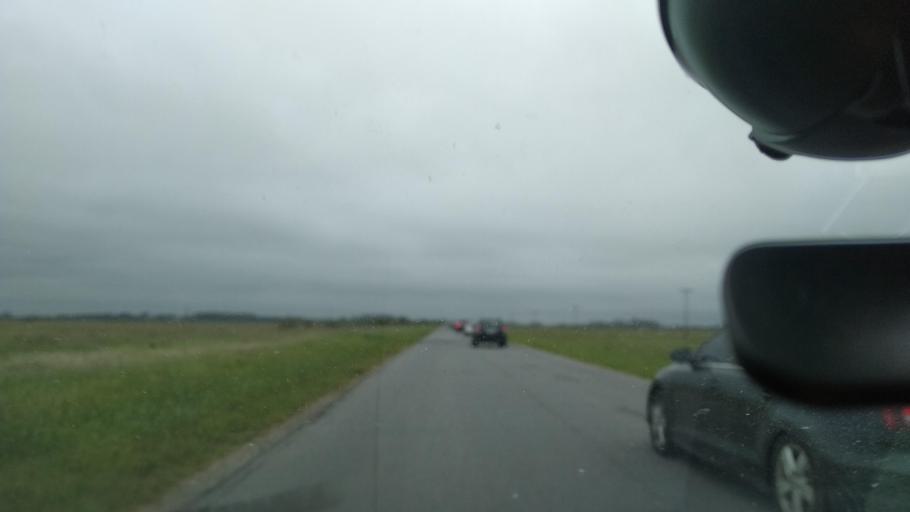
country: AR
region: Buenos Aires
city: Veronica
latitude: -35.5535
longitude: -57.3074
